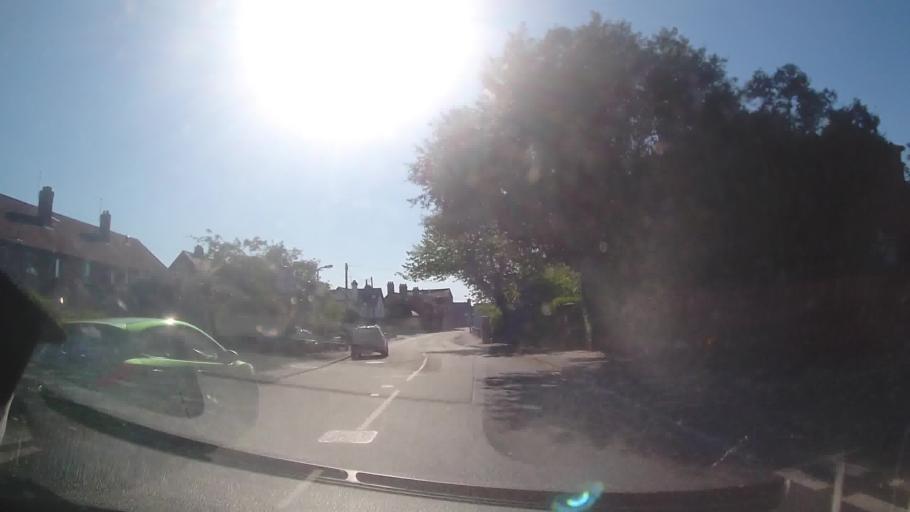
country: GB
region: England
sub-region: Shropshire
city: Wem
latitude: 52.8552
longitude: -2.7292
